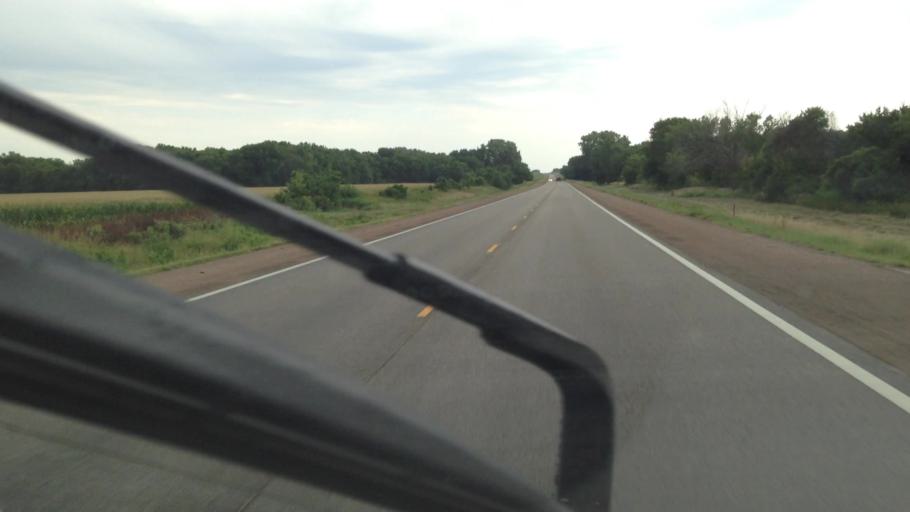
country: US
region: Kansas
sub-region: Woodson County
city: Yates Center
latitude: 38.0321
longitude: -95.7390
